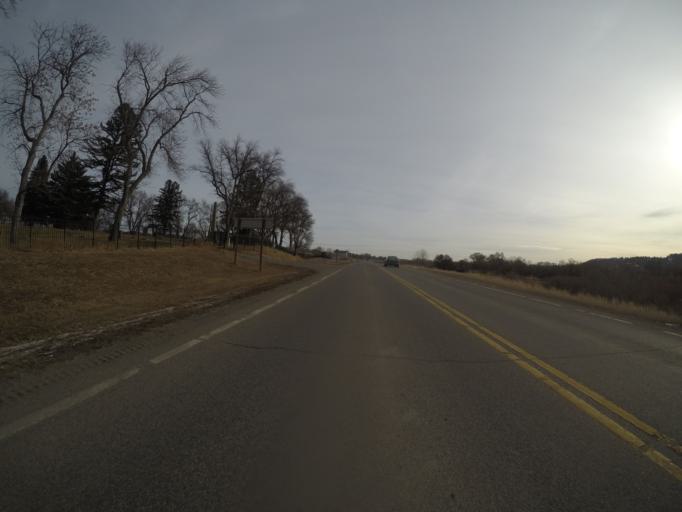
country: US
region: Montana
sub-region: Stillwater County
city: Columbus
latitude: 45.6412
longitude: -109.2738
